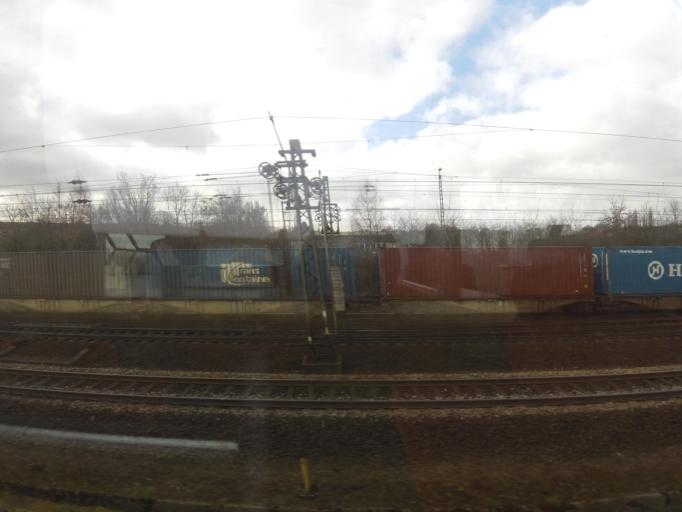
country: DE
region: Hamburg
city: Harburg
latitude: 53.4421
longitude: 10.0095
